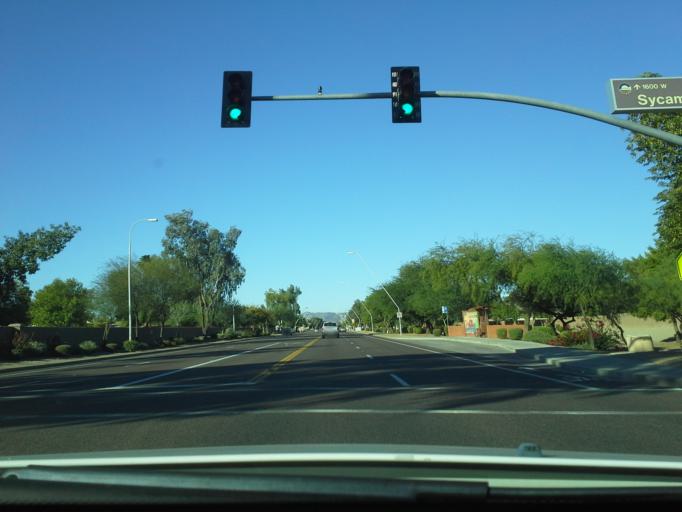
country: US
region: Arizona
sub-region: Maricopa County
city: San Carlos
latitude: 33.3496
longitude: -111.8700
